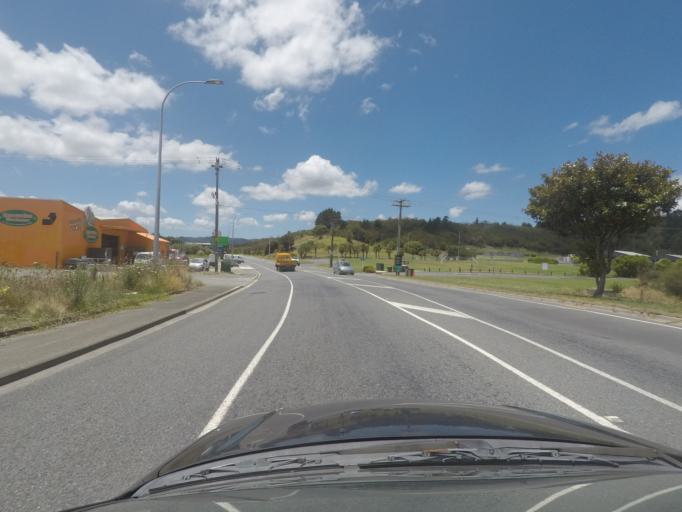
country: NZ
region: Northland
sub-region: Whangarei
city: Whangarei
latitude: -35.7442
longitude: 174.3274
